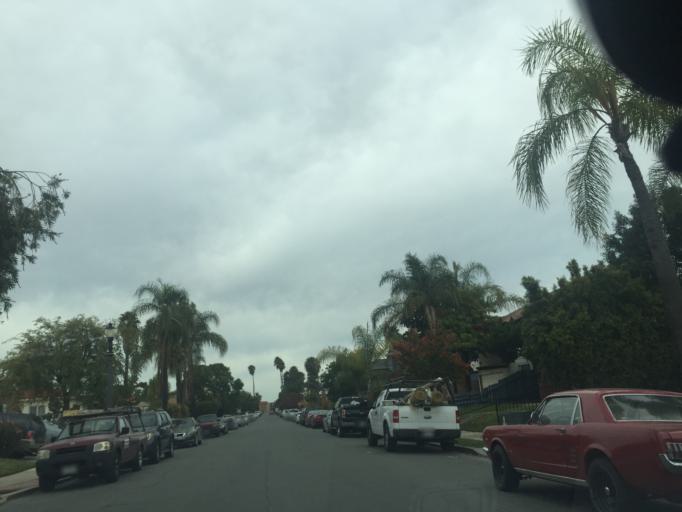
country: US
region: California
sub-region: San Diego County
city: Lemon Grove
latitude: 32.7578
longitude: -117.0847
